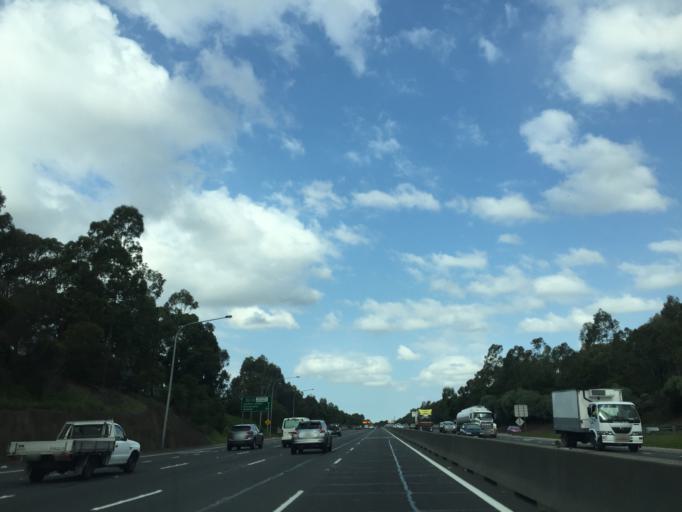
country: AU
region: New South Wales
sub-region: Holroyd
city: Merrylands
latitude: -33.8199
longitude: 150.9830
